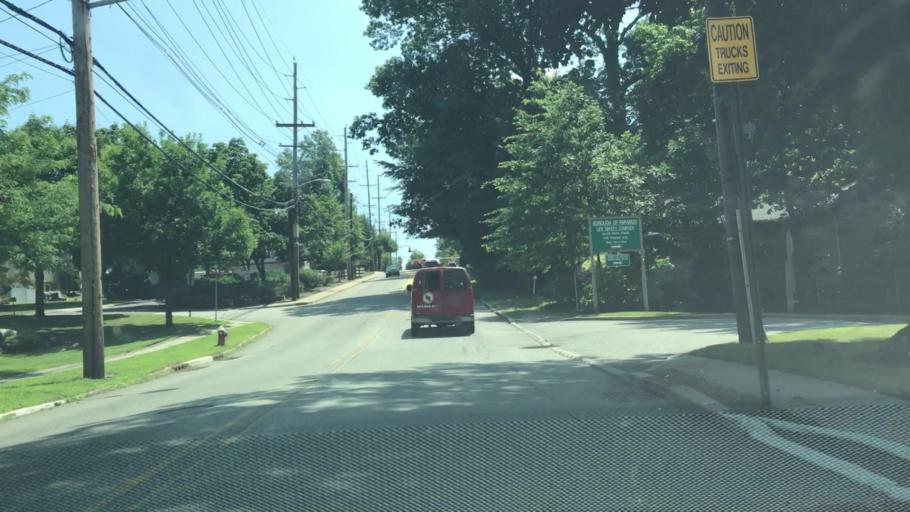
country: US
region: New Jersey
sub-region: Bergen County
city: Paramus
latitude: 40.9288
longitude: -74.0682
